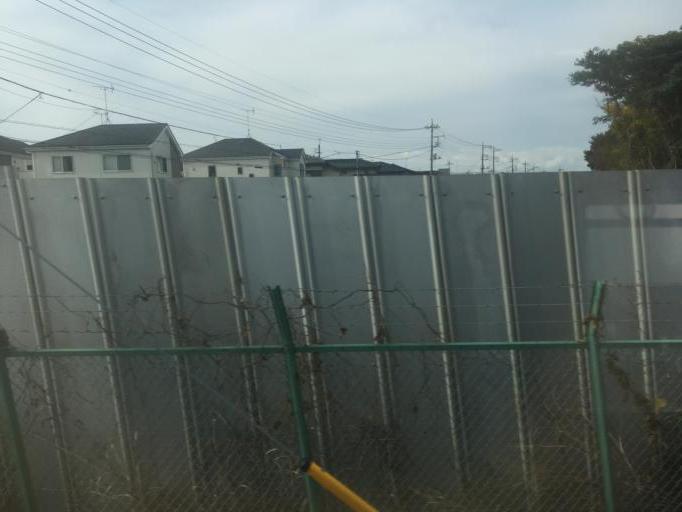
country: JP
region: Saitama
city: Sayama
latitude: 35.8342
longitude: 139.4093
